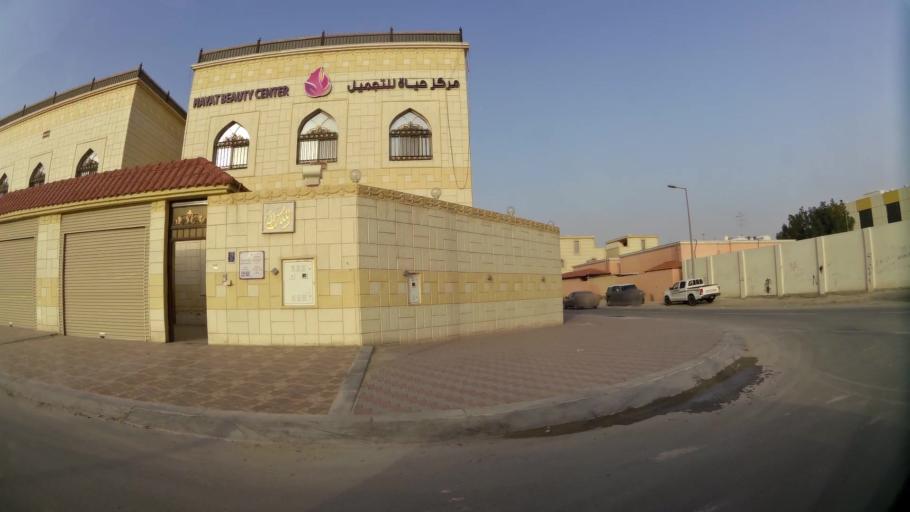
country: QA
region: Baladiyat ar Rayyan
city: Ar Rayyan
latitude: 25.2371
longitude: 51.4486
